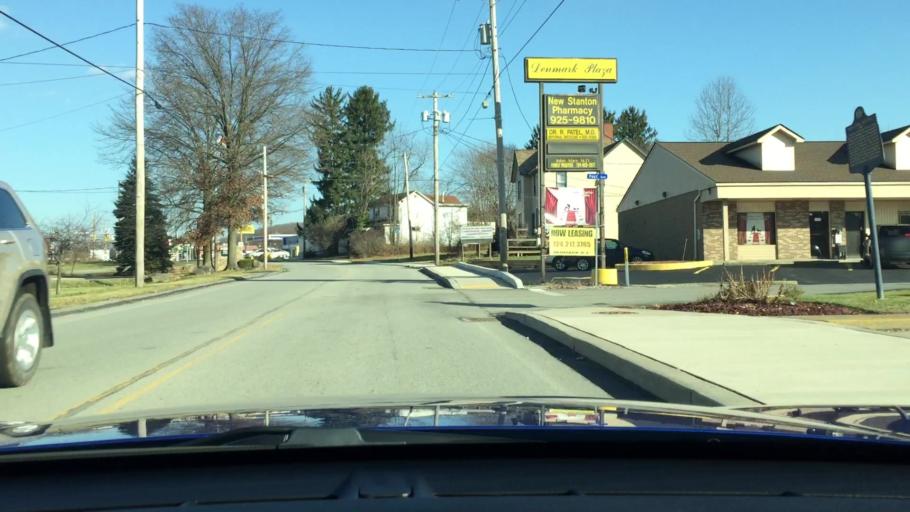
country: US
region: Pennsylvania
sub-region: Westmoreland County
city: New Stanton
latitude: 40.2160
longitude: -79.6100
